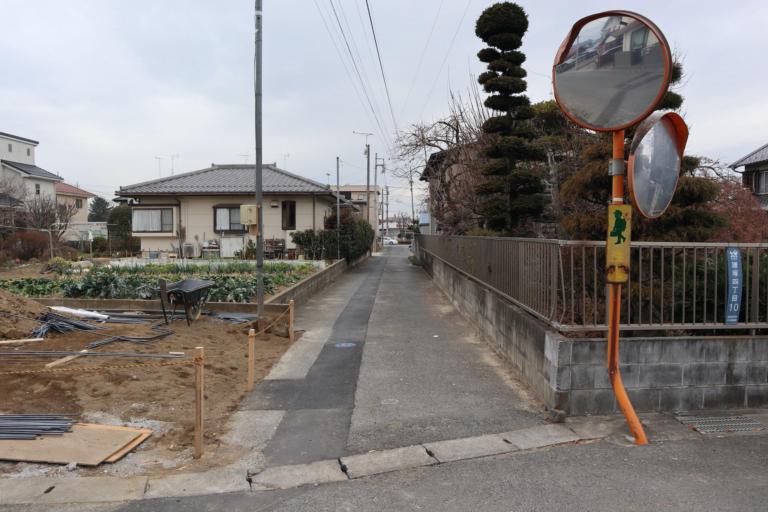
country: JP
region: Saitama
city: Fukiage-fujimi
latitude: 36.1095
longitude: 139.4496
